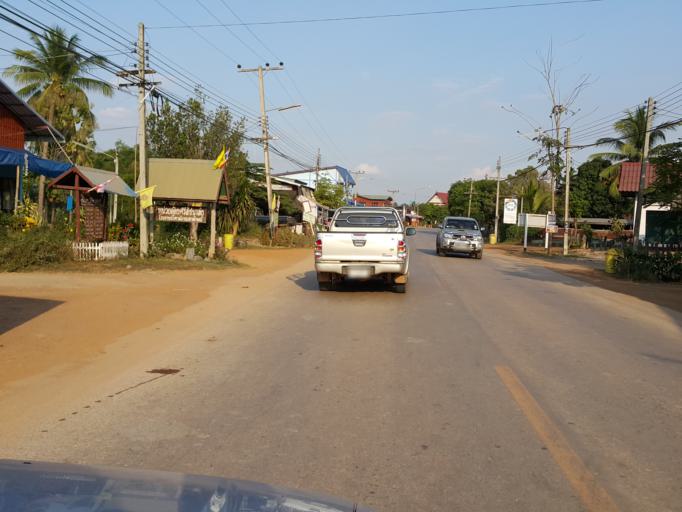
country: TH
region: Sukhothai
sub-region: Amphoe Si Satchanalai
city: Si Satchanalai
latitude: 17.4343
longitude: 99.7217
